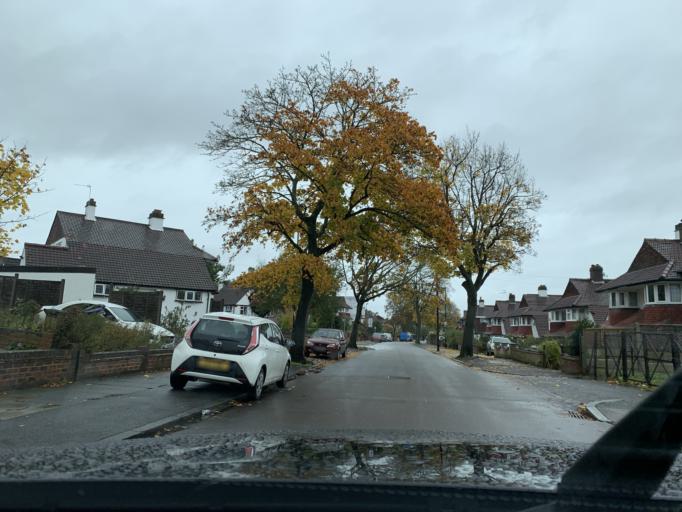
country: GB
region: England
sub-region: Greater London
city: Blackheath
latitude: 51.4384
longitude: 0.0232
